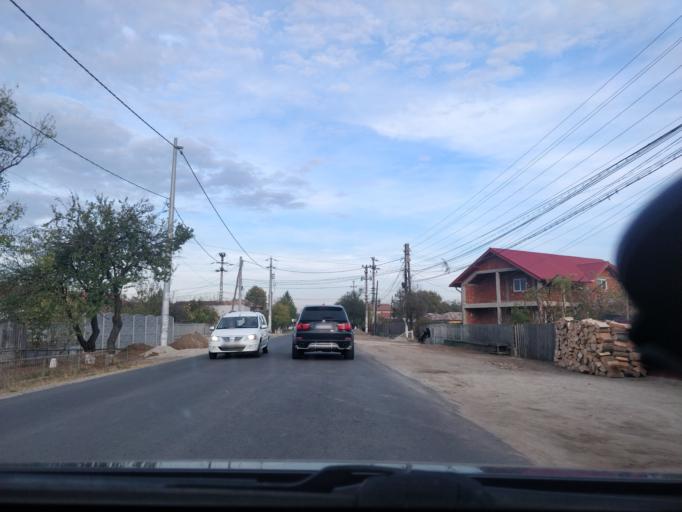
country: RO
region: Giurgiu
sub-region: Comuna Bolintin Vale
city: Malu Spart
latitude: 44.4413
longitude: 25.7087
